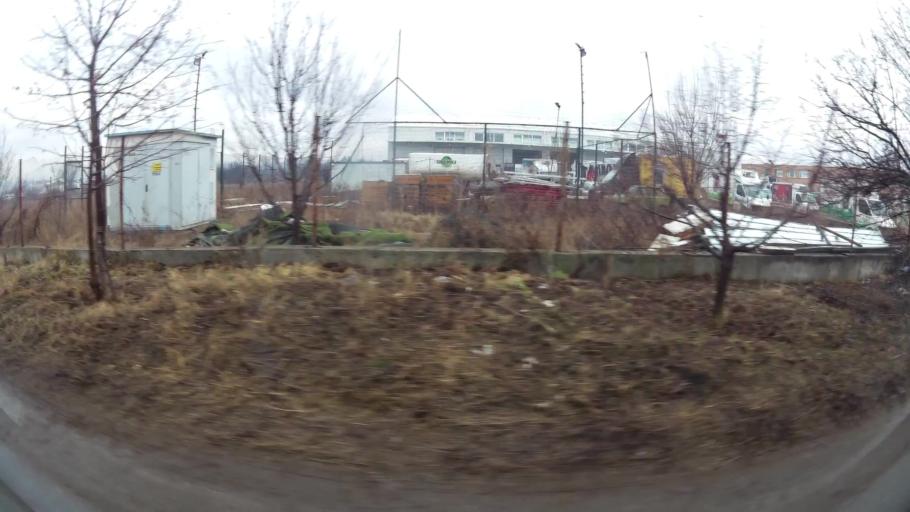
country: BG
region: Sofia-Capital
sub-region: Stolichna Obshtina
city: Sofia
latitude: 42.7078
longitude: 23.4294
